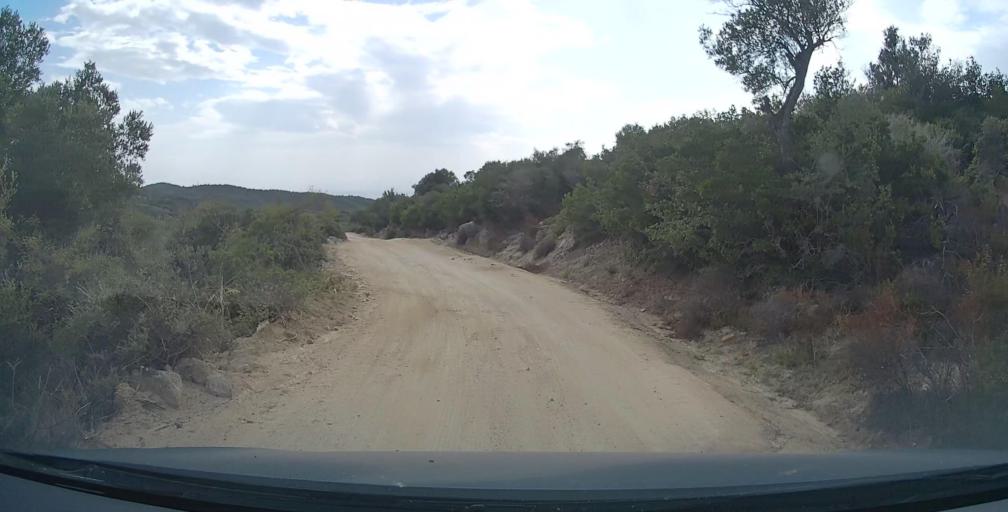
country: GR
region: Central Macedonia
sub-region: Nomos Chalkidikis
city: Sykia
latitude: 40.0106
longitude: 23.9280
